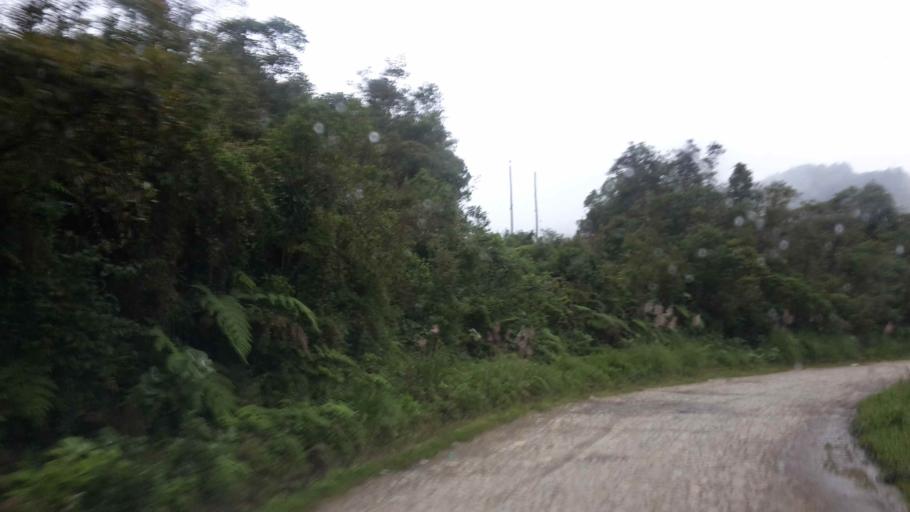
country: BO
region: Cochabamba
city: Colomi
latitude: -17.1601
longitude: -65.9052
